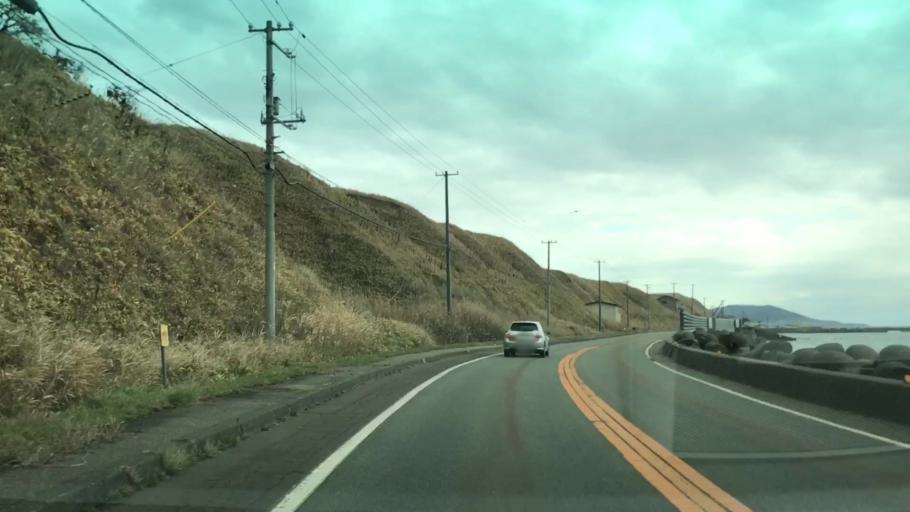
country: JP
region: Hokkaido
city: Shizunai-furukawacho
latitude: 42.0504
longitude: 143.0950
